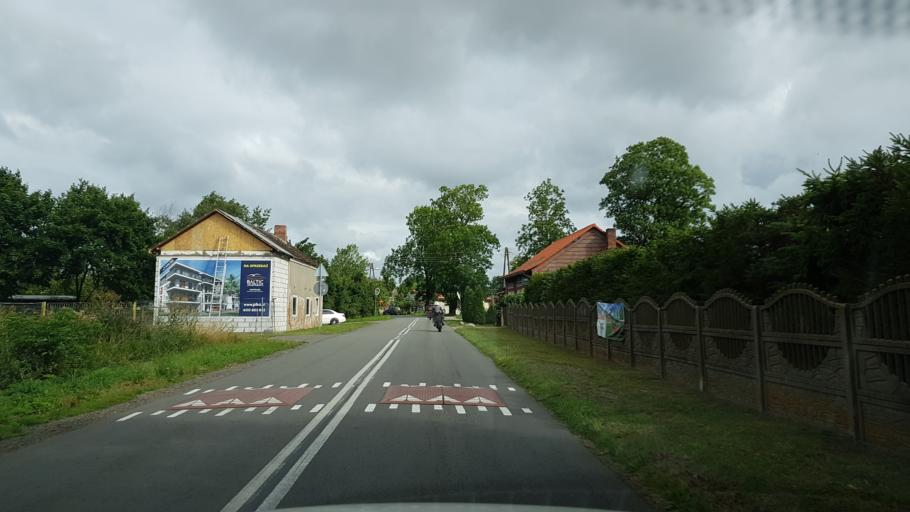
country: PL
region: West Pomeranian Voivodeship
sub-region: Powiat gryficki
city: Rewal
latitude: 54.0557
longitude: 15.0274
